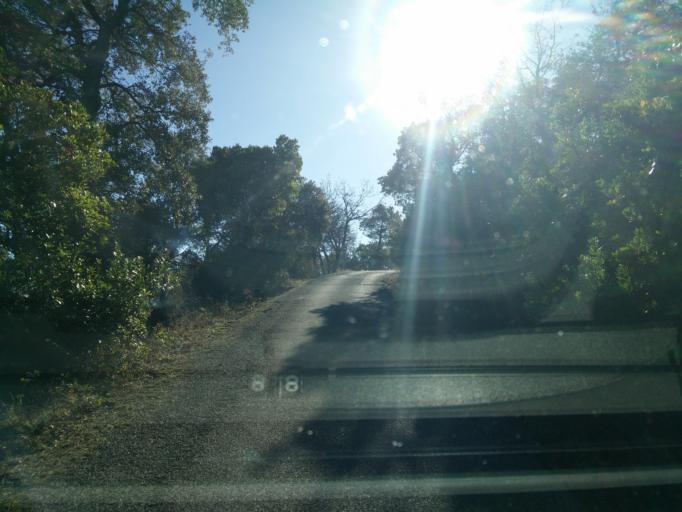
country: FR
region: Provence-Alpes-Cote d'Azur
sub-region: Departement du Var
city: Gonfaron
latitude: 43.2796
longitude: 6.2971
